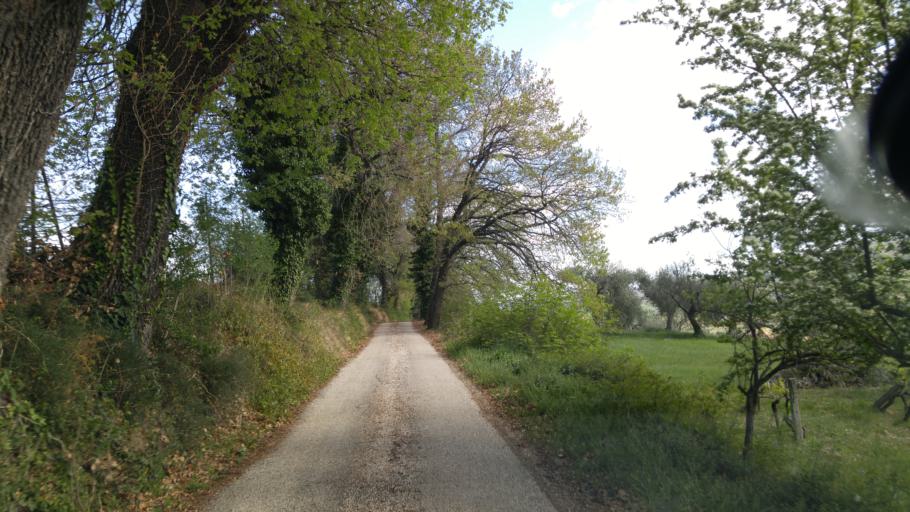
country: IT
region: The Marches
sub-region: Provincia di Pesaro e Urbino
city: Fenile
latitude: 43.8462
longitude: 12.9608
